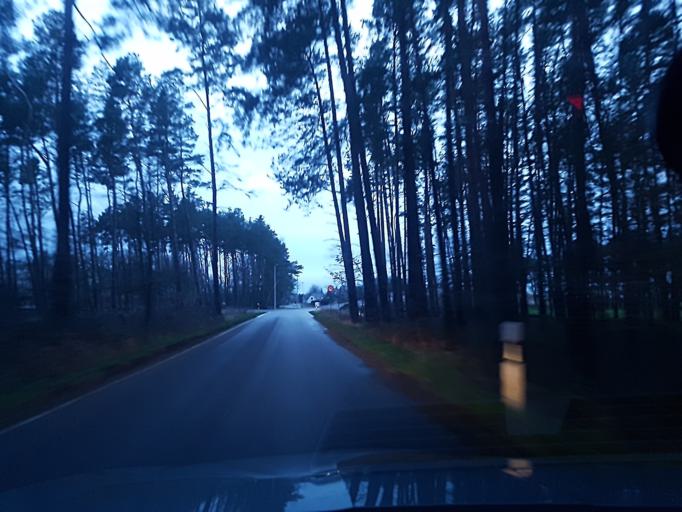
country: DE
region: Brandenburg
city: Ruckersdorf
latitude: 51.5782
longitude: 13.5764
